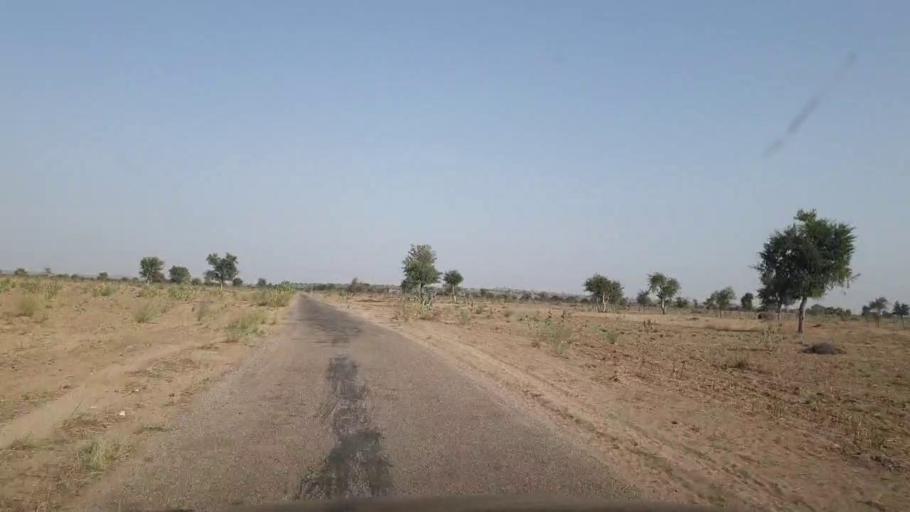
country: PK
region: Sindh
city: Islamkot
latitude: 25.1322
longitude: 70.4751
